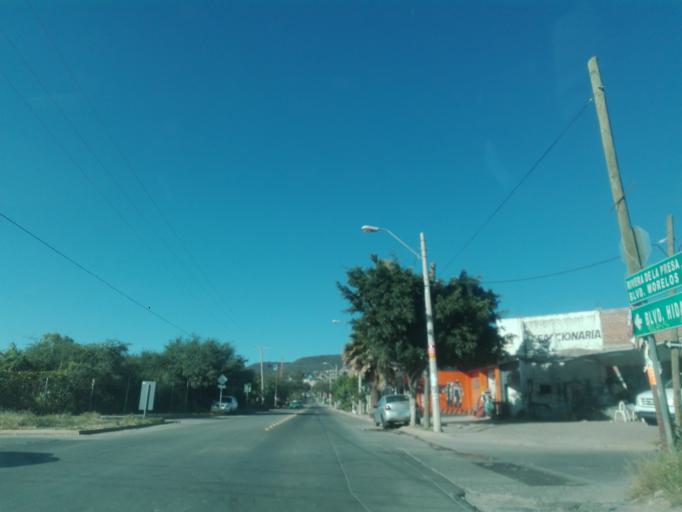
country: MX
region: Guanajuato
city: Leon
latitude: 21.1927
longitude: -101.6795
